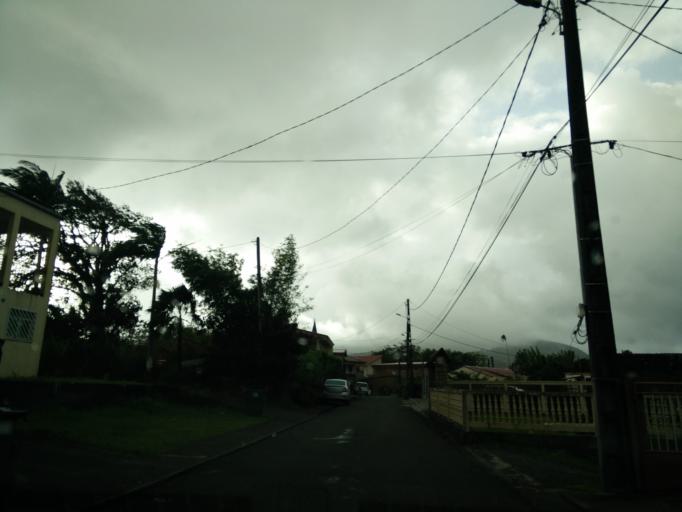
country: MQ
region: Martinique
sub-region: Martinique
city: Le Morne-Rouge
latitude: 14.7731
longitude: -61.1335
